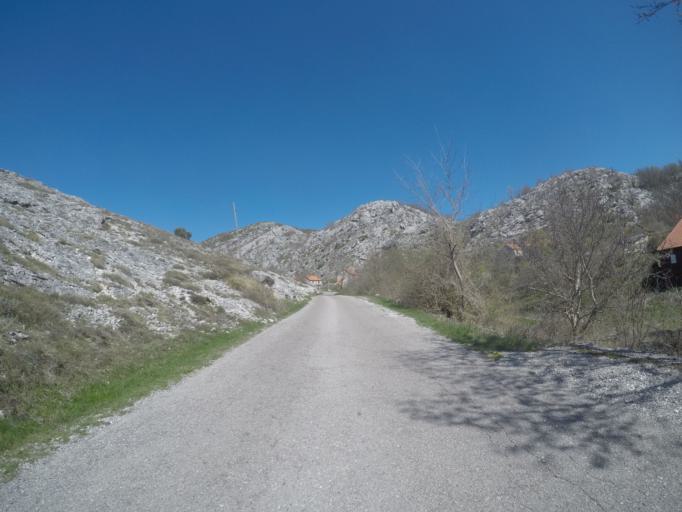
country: ME
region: Cetinje
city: Cetinje
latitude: 42.4573
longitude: 18.8735
